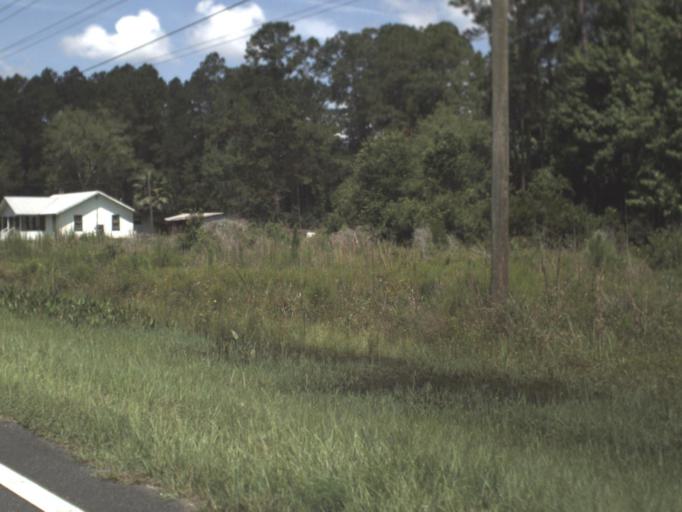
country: US
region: Florida
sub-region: Levy County
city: Chiefland
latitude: 29.3159
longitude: -82.7896
